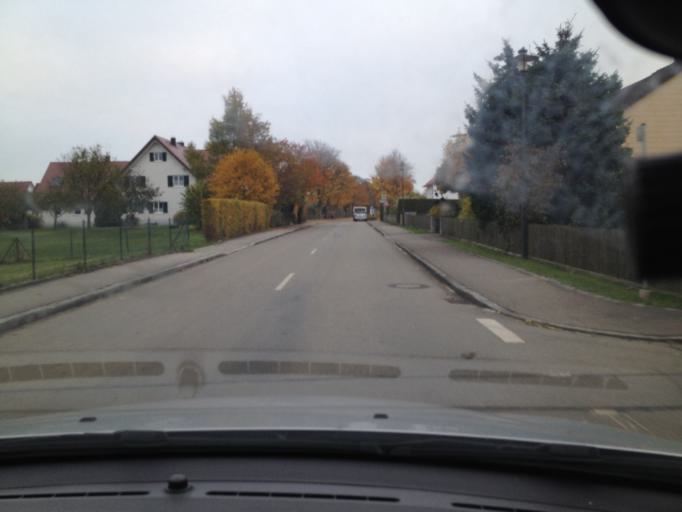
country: DE
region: Bavaria
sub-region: Swabia
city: Kleinaitingen
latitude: 48.2155
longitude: 10.8426
